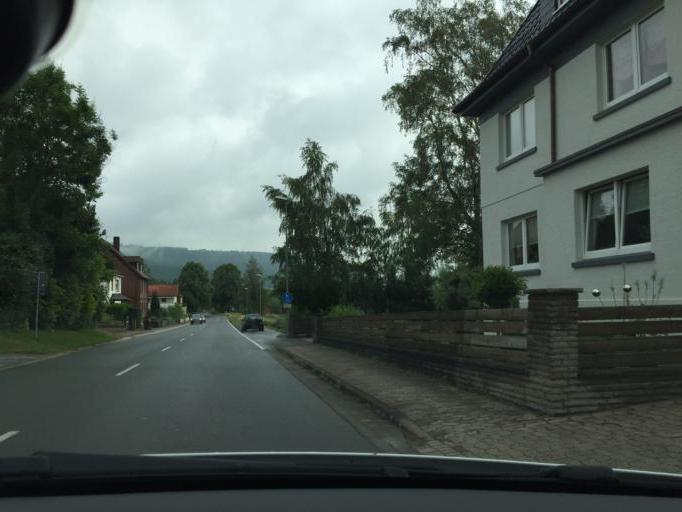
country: DE
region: Lower Saxony
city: Vahlbruch
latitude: 52.0025
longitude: 9.3387
